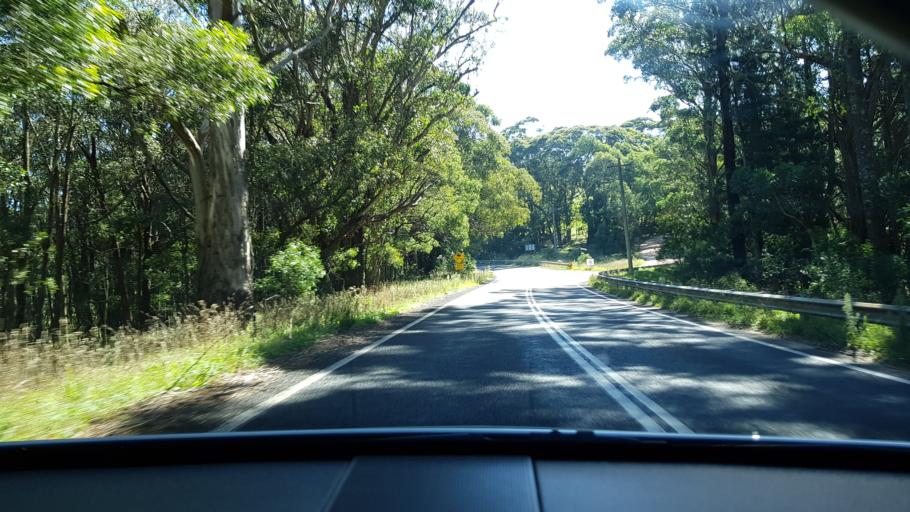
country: AU
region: New South Wales
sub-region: Lithgow
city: Bowenfels
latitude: -33.6394
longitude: 150.0566
